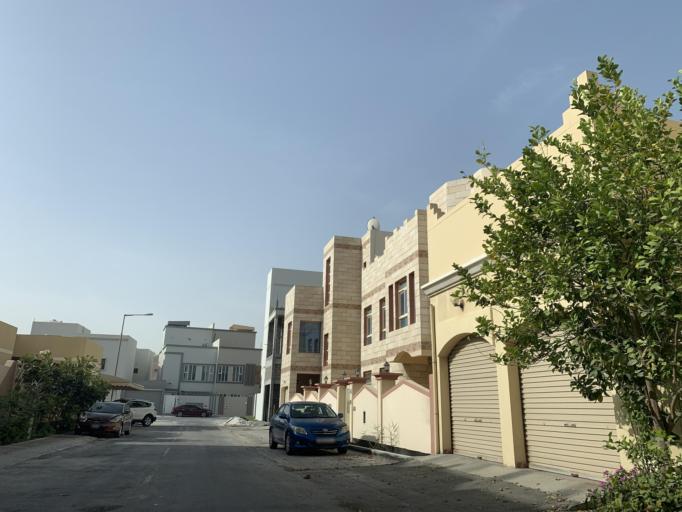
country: BH
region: Northern
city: Madinat `Isa
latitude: 26.1818
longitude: 50.5633
